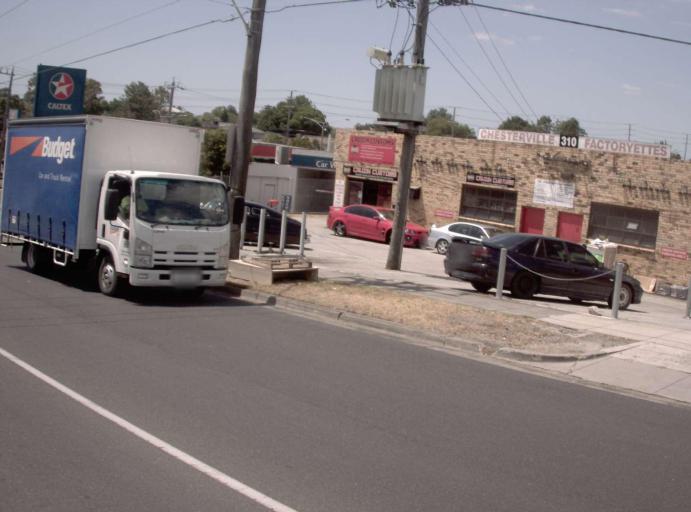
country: AU
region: Victoria
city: Highett
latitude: -37.9372
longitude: 145.0611
